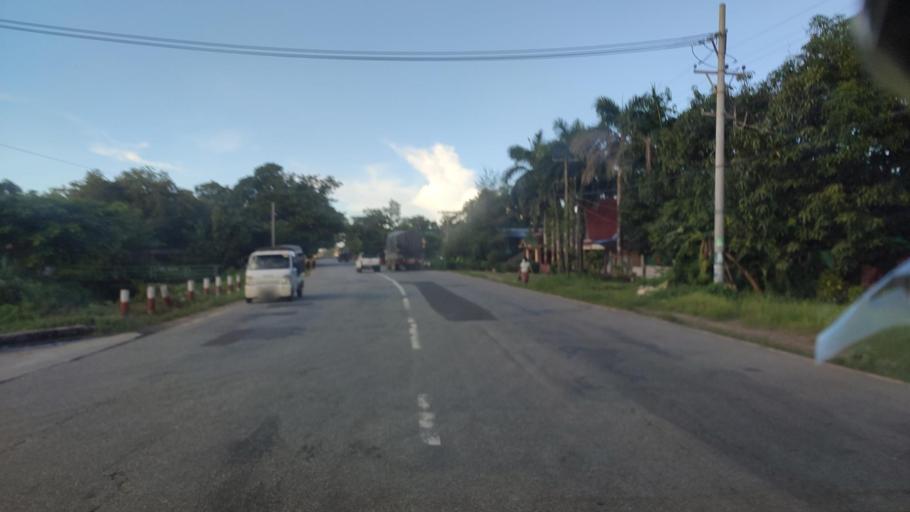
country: MM
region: Bago
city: Bago
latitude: 17.5789
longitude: 96.5568
